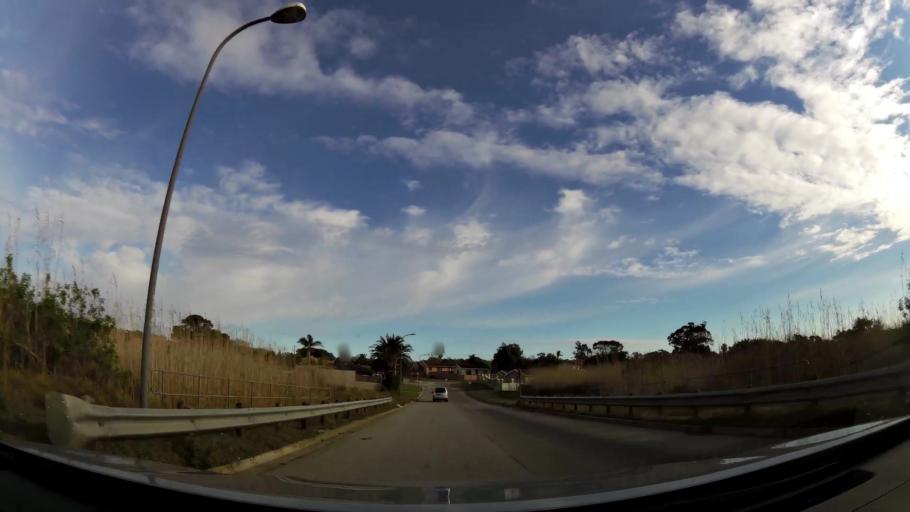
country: ZA
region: Eastern Cape
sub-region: Nelson Mandela Bay Metropolitan Municipality
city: Port Elizabeth
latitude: -33.9629
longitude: 25.4764
